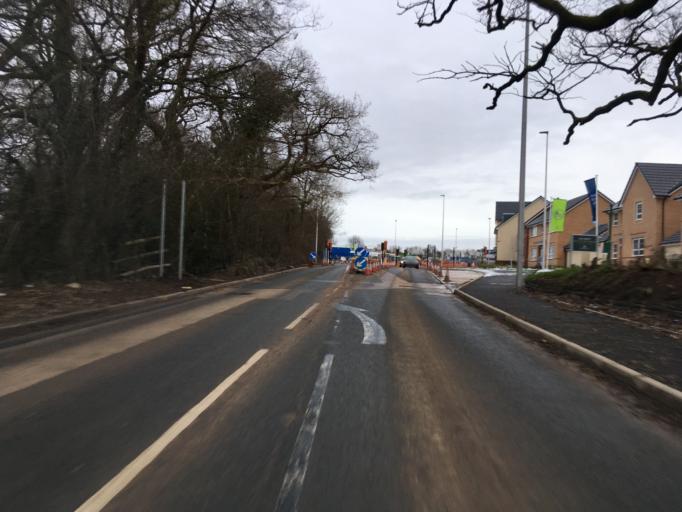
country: GB
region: Wales
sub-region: Cardiff
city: Radyr
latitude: 51.5105
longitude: -3.2692
